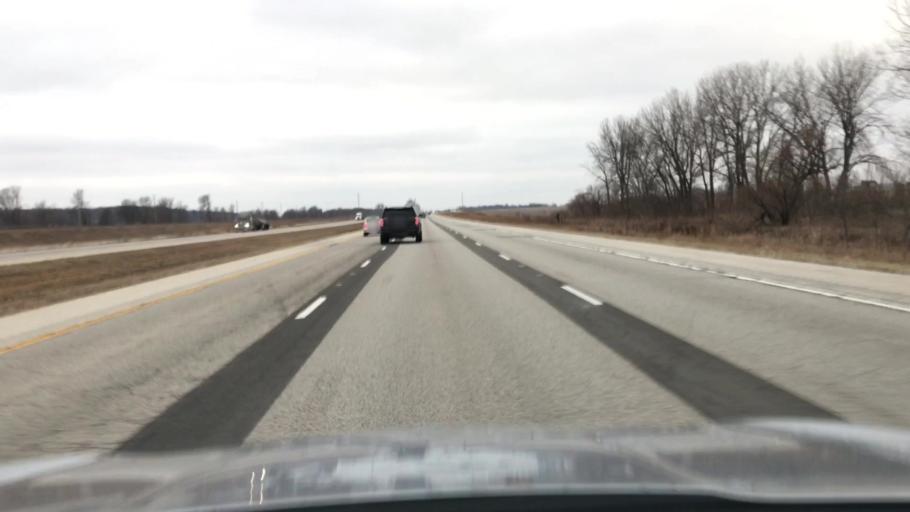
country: US
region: Illinois
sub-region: Sangamon County
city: Williamsville
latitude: 40.0429
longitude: -89.4654
